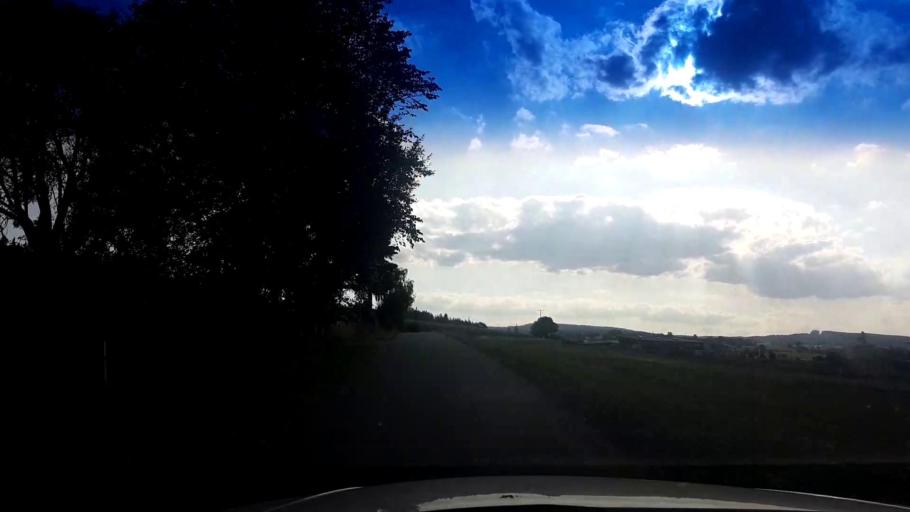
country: DE
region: Bavaria
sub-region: Upper Palatinate
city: Krummennaab
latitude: 49.8312
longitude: 12.0740
